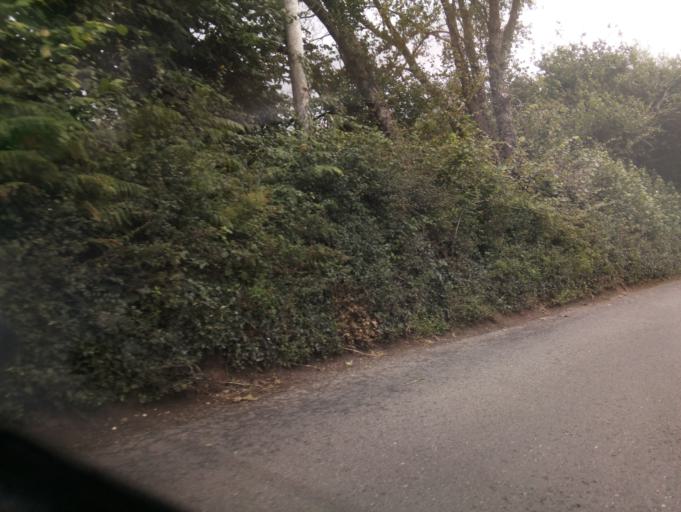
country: GB
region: England
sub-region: Devon
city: Kingsbridge
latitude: 50.2738
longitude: -3.7051
